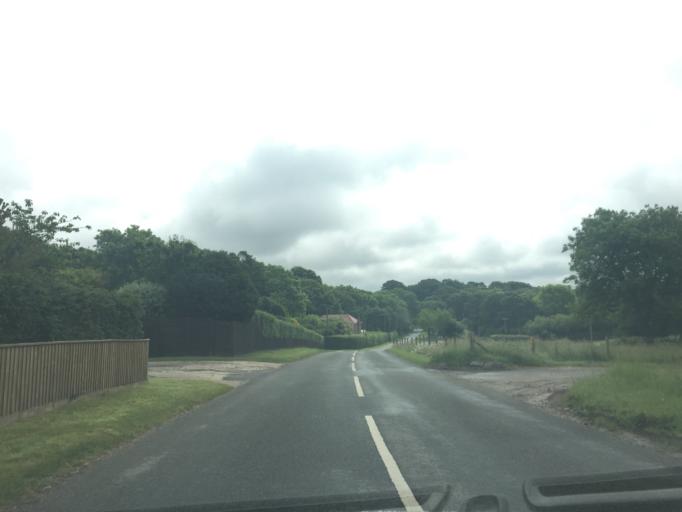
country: GB
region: England
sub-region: Dorset
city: Bovington Camp
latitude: 50.7202
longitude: -2.2913
